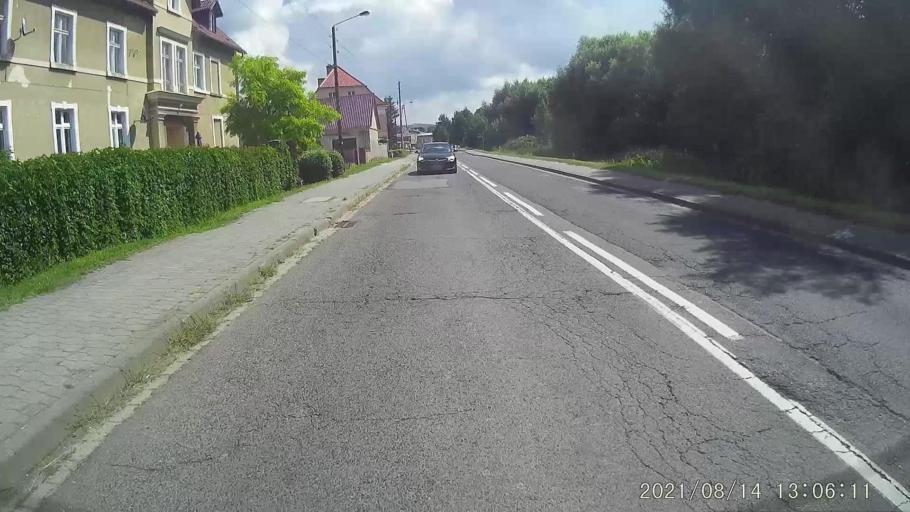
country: PL
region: Lower Silesian Voivodeship
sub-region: Powiat klodzki
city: Klodzko
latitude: 50.3608
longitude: 16.7191
